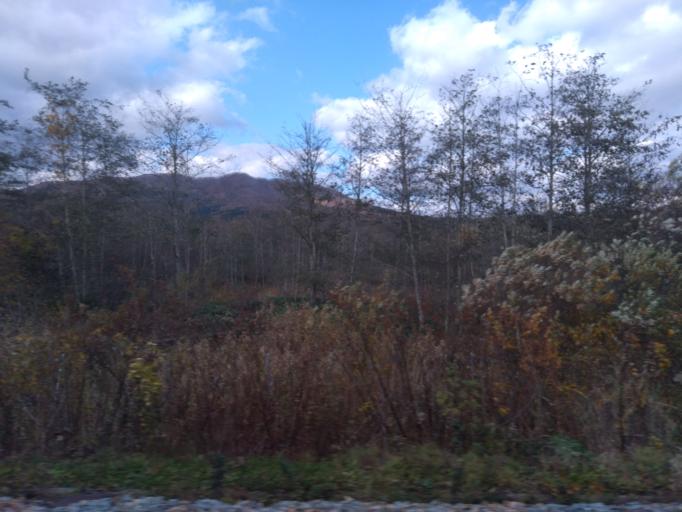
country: JP
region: Hokkaido
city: Shiraoi
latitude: 42.4615
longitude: 141.2016
